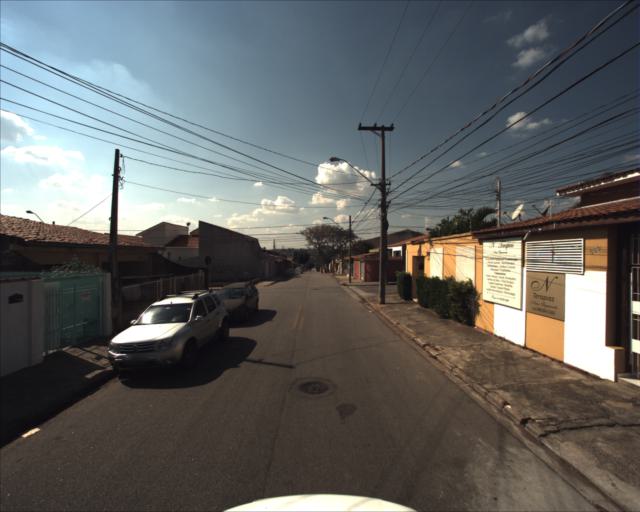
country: BR
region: Sao Paulo
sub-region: Sorocaba
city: Sorocaba
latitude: -23.4780
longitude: -47.4500
